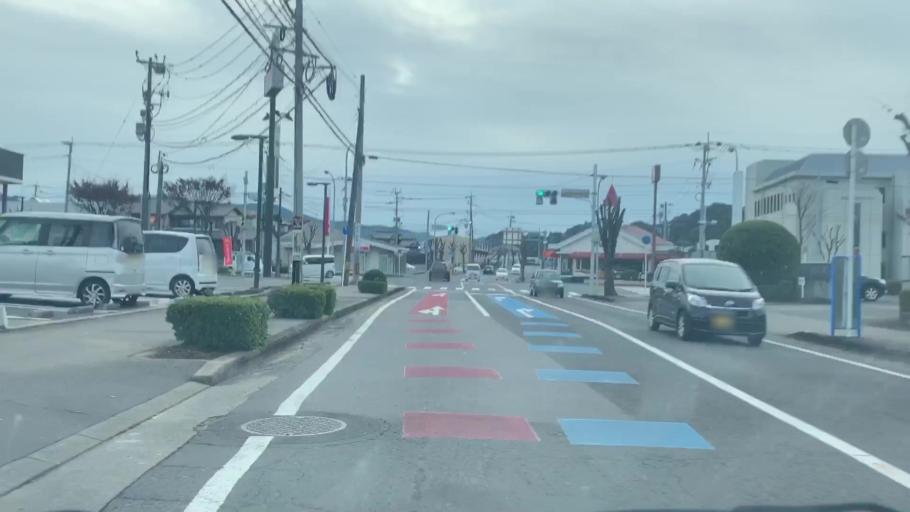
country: JP
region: Saga Prefecture
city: Takeocho-takeo
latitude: 33.1953
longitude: 130.0289
